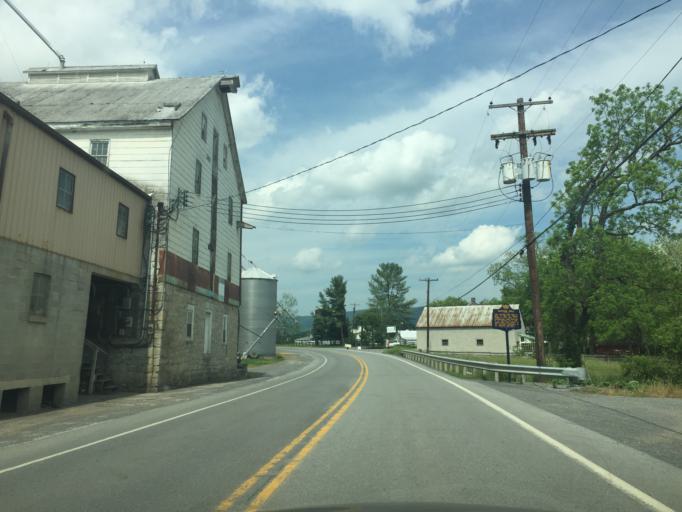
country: US
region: Pennsylvania
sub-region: Fulton County
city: McConnellsburg
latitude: 39.8595
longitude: -78.0364
